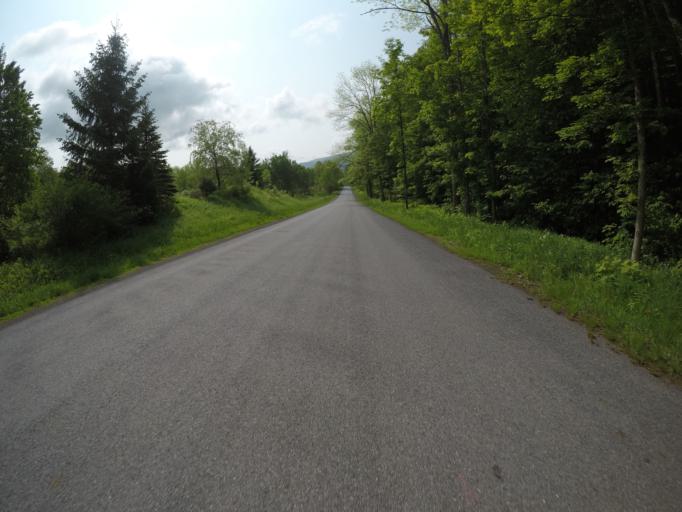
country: US
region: New York
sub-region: Delaware County
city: Stamford
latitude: 42.1625
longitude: -74.6629
